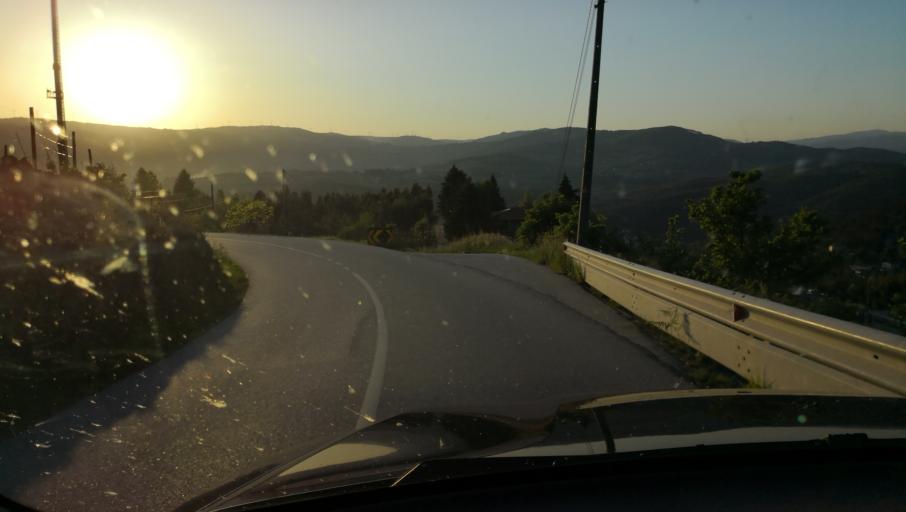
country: PT
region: Vila Real
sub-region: Mondim de Basto
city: Mondim de Basto
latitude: 41.4119
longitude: -7.9345
